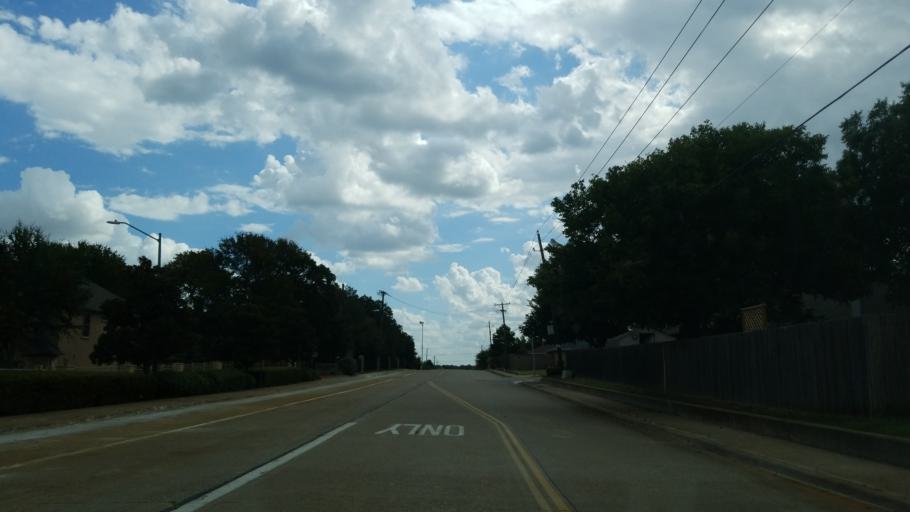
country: US
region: Texas
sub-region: Tarrant County
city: Euless
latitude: 32.8744
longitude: -97.0738
